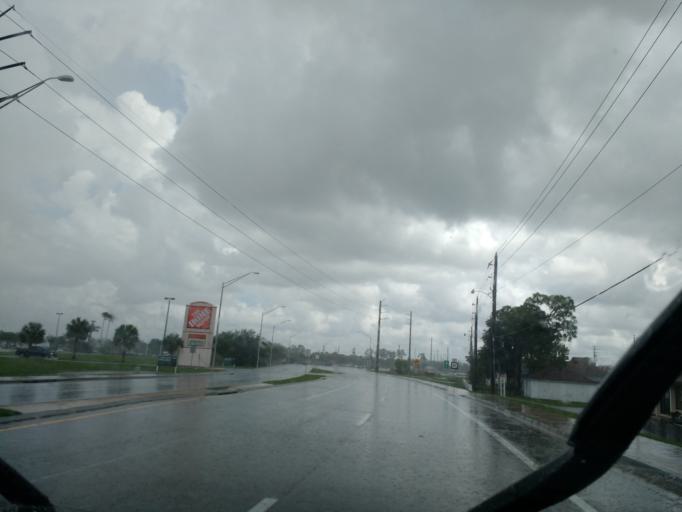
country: US
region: Florida
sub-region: Charlotte County
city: Charlotte Park
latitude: 26.8883
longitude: -82.0232
